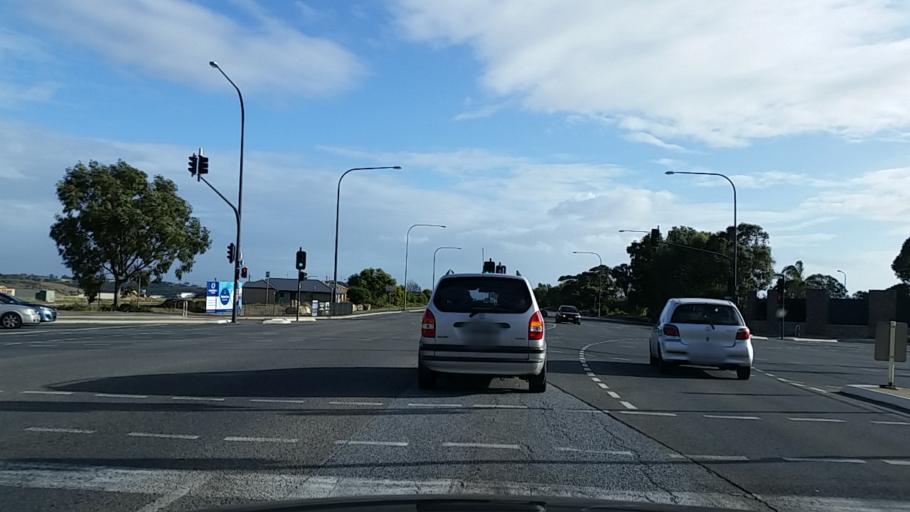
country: AU
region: South Australia
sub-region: Marion
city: Happy Valley
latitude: -35.0792
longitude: 138.5169
